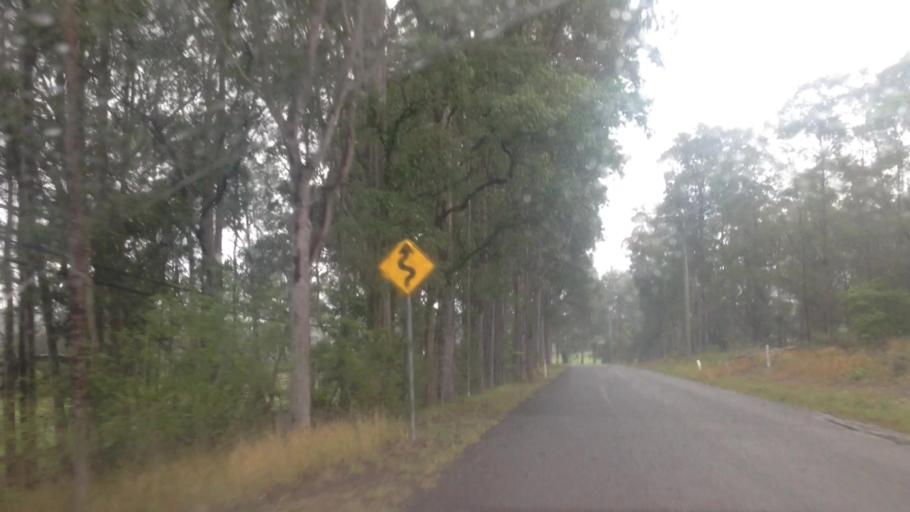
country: AU
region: New South Wales
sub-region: Wyong Shire
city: Little Jilliby
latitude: -33.2126
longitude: 151.3713
